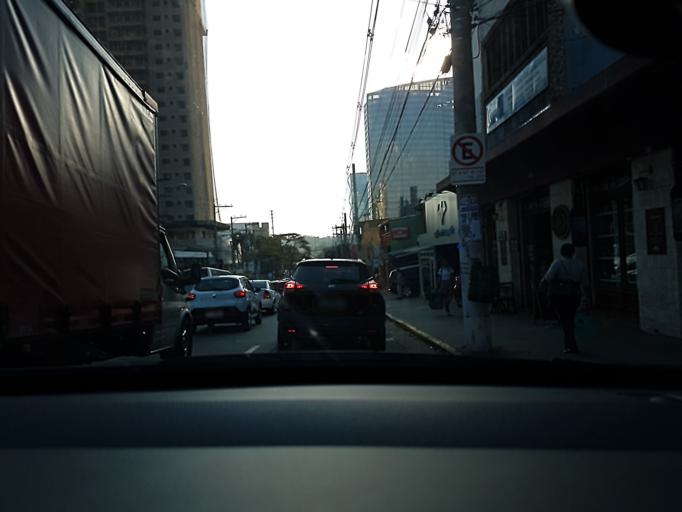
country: BR
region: Sao Paulo
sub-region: Sao Paulo
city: Sao Paulo
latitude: -23.6196
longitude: -46.6949
